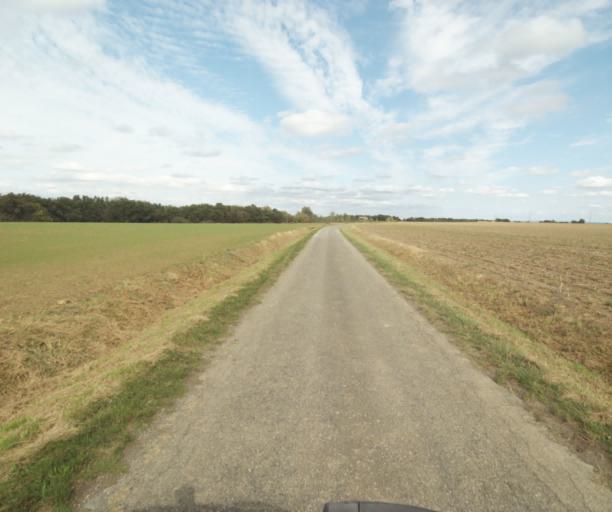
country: FR
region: Midi-Pyrenees
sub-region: Departement du Tarn-et-Garonne
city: Finhan
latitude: 43.8774
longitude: 1.1722
